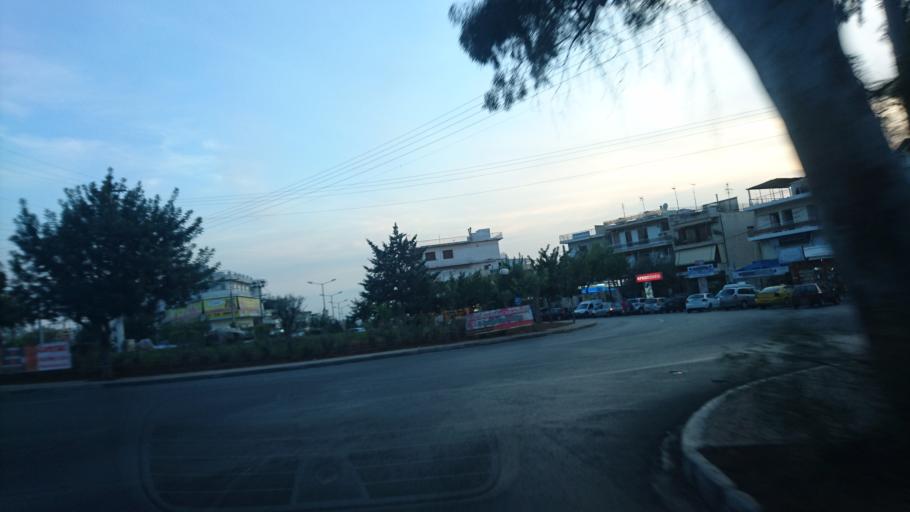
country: GR
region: Attica
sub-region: Nomarchia Athinas
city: Ilioupoli
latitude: 37.9362
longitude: 23.7586
